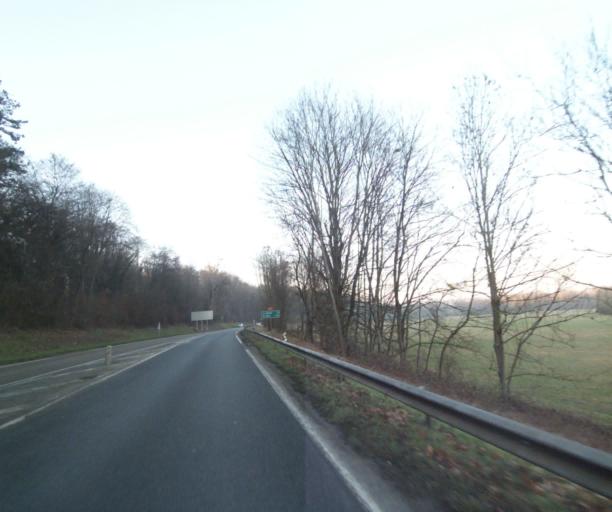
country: FR
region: Champagne-Ardenne
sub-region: Departement de la Haute-Marne
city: Bienville
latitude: 48.5939
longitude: 5.0310
